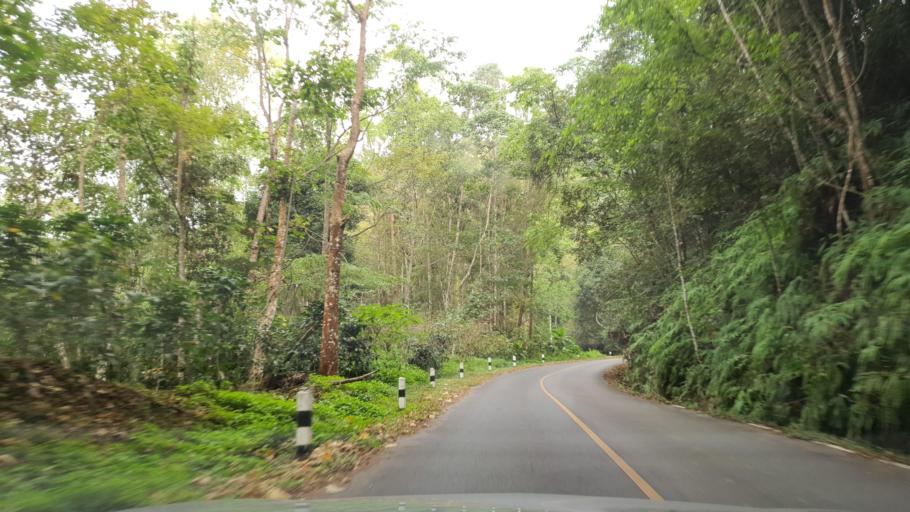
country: TH
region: Chiang Mai
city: Mae On
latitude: 18.9406
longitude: 99.3611
